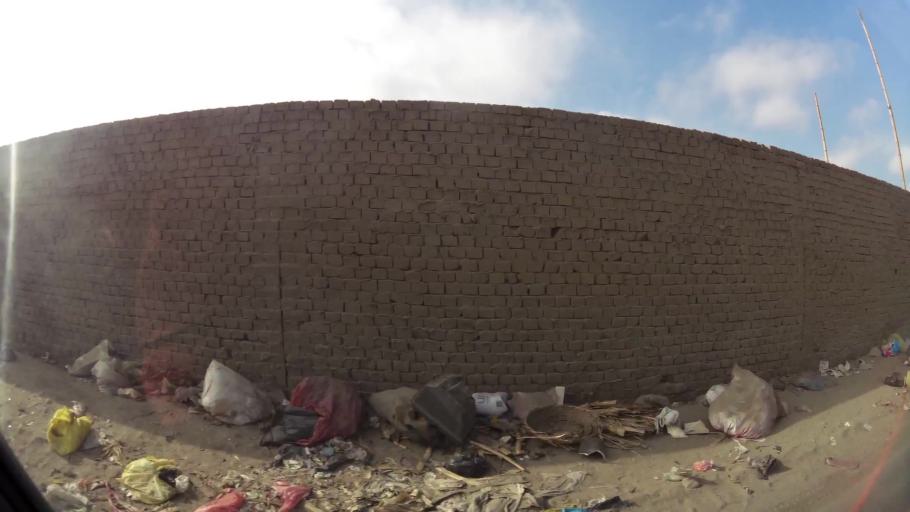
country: PE
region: La Libertad
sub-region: Provincia de Trujillo
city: La Esperanza
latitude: -8.0935
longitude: -79.0298
